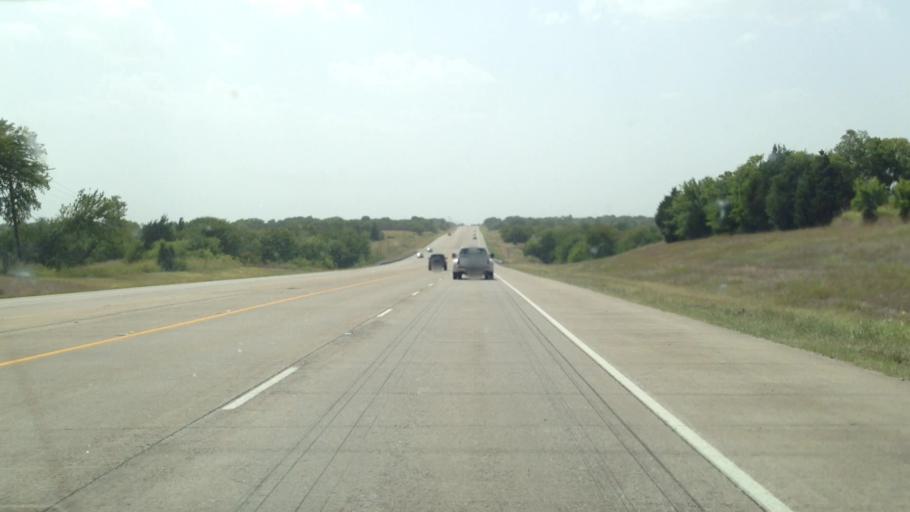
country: US
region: Texas
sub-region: Collin County
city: Princeton
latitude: 33.1687
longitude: -96.4660
